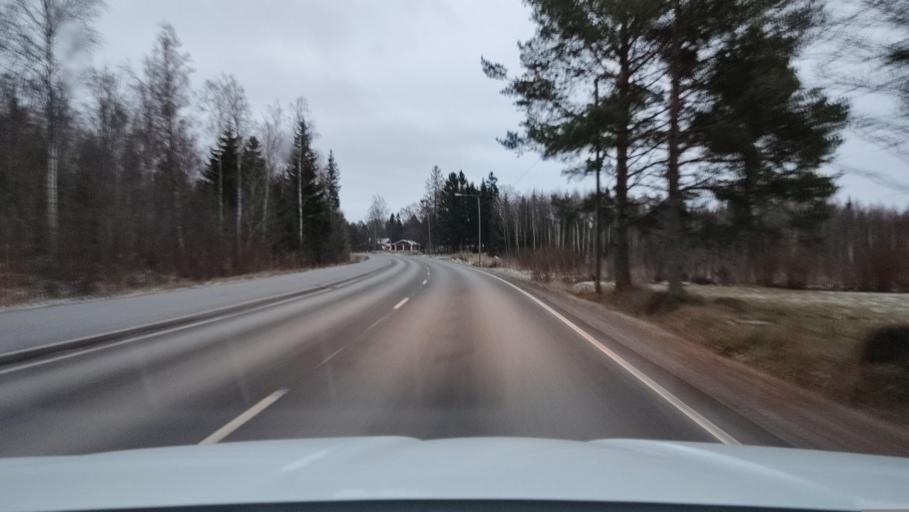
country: FI
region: Ostrobothnia
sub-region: Vaasa
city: Replot
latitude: 63.2214
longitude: 21.4144
